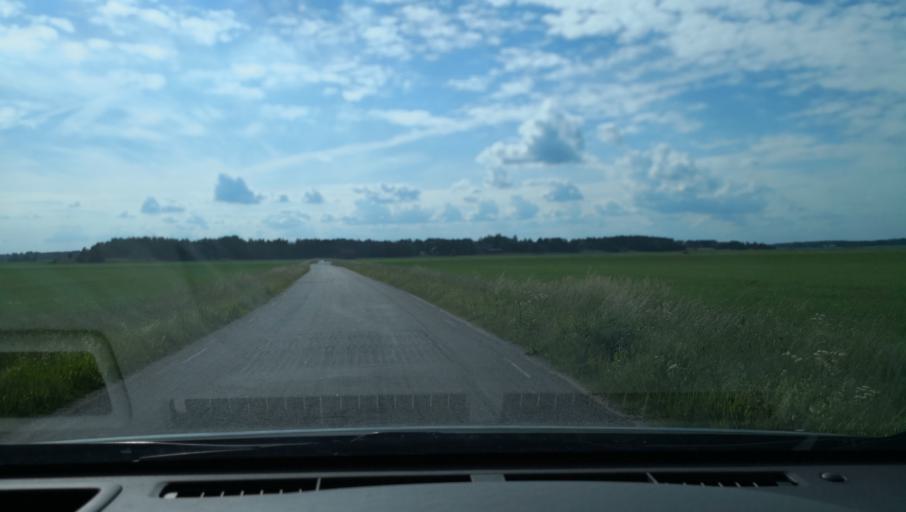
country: SE
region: Uppsala
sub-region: Enkopings Kommun
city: Irsta
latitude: 59.7527
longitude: 16.9678
